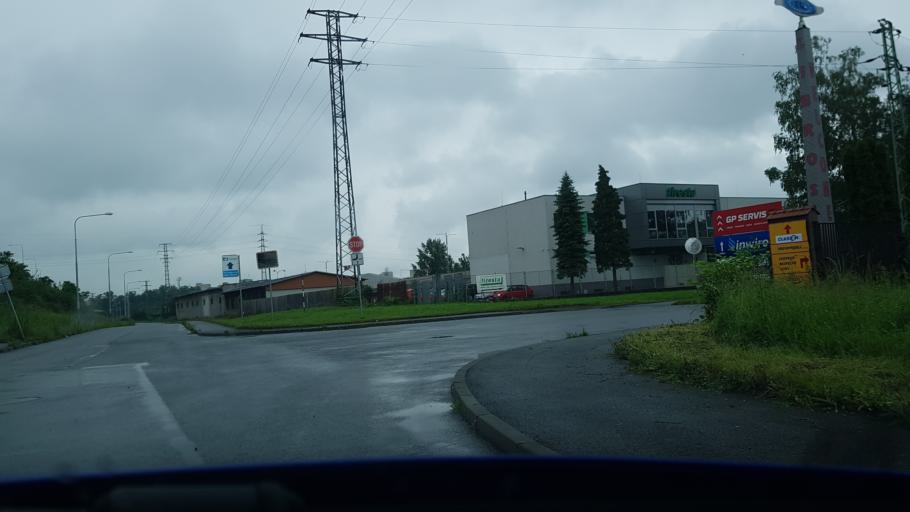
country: CZ
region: Moravskoslezsky
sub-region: Okres Ostrava-Mesto
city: Ostrava
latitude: 49.8509
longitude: 18.2563
